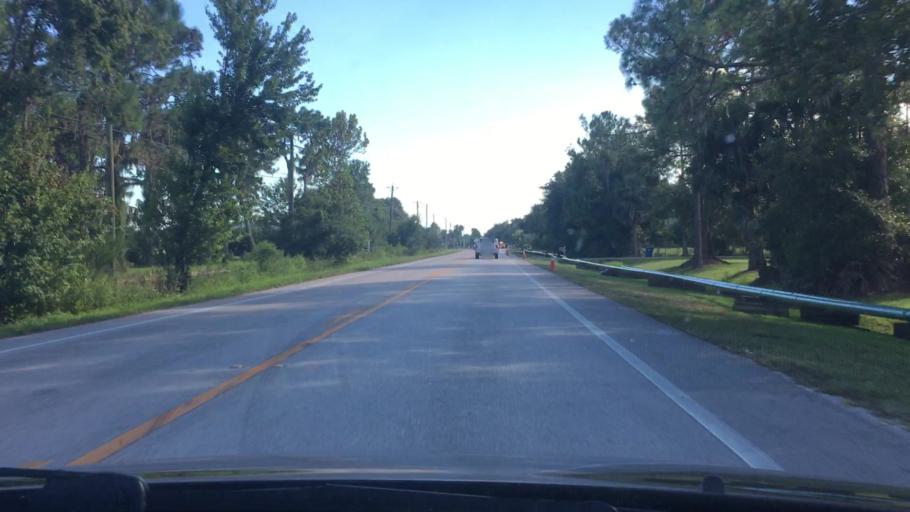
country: US
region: Florida
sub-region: Volusia County
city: Samsula-Spruce Creek
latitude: 29.0934
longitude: -81.0687
